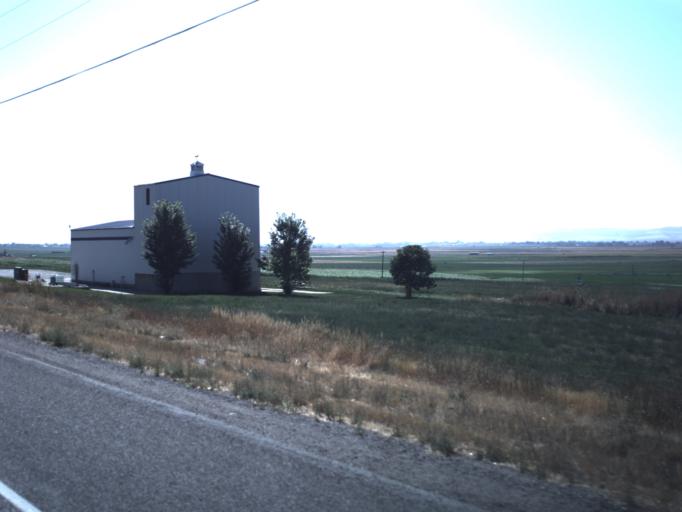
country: US
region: Utah
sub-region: Cache County
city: Richmond
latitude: 41.9092
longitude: -111.8148
